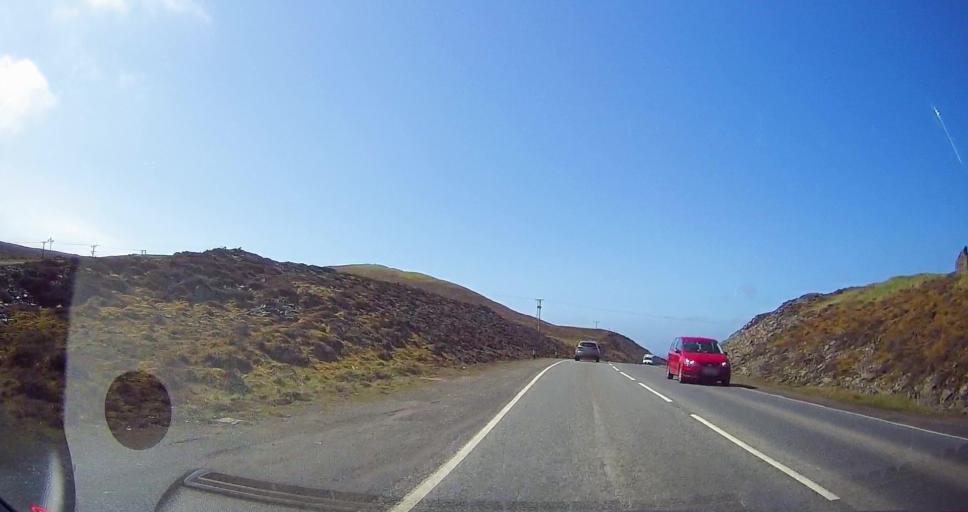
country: GB
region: Scotland
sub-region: Shetland Islands
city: Lerwick
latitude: 60.1408
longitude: -1.2553
